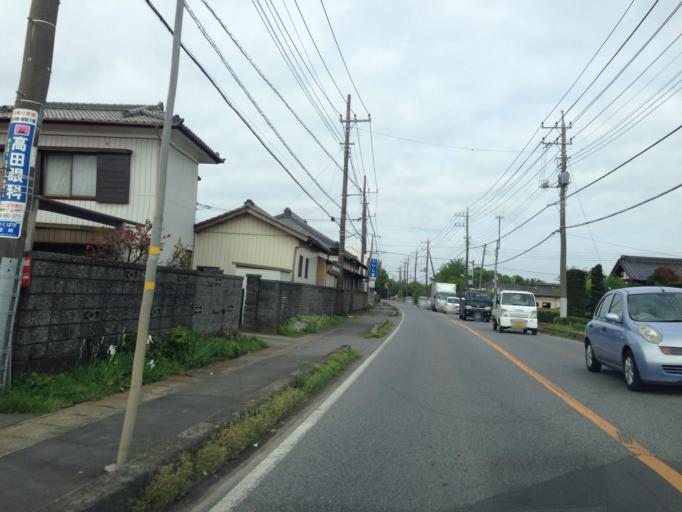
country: JP
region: Ibaraki
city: Tsukuba
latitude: 36.1352
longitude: 140.0710
